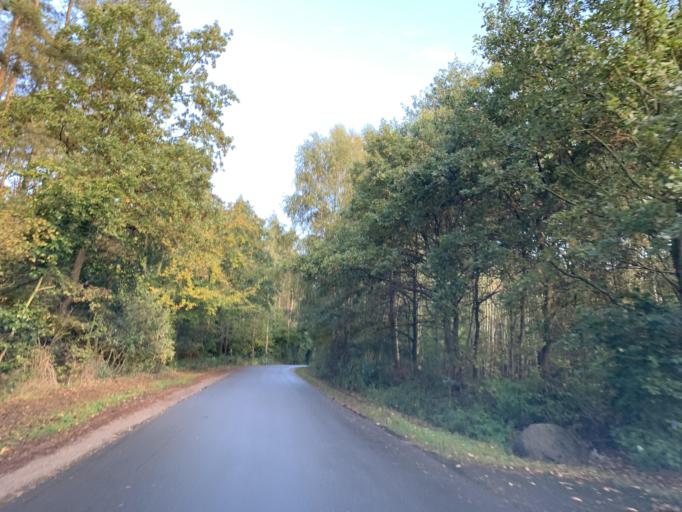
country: DE
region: Mecklenburg-Vorpommern
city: Blankensee
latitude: 53.4303
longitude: 13.2637
